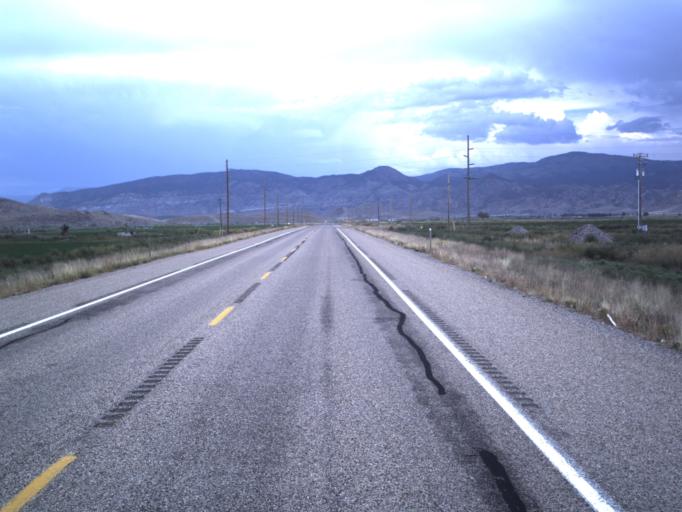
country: US
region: Utah
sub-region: Piute County
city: Junction
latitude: 38.1768
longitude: -112.2537
